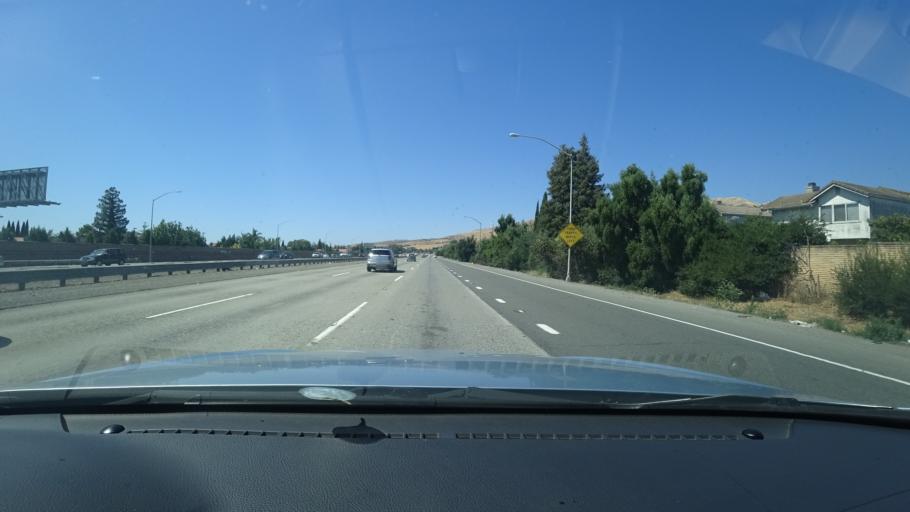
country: US
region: California
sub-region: Santa Clara County
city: Milpitas
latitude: 37.4403
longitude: -121.8896
